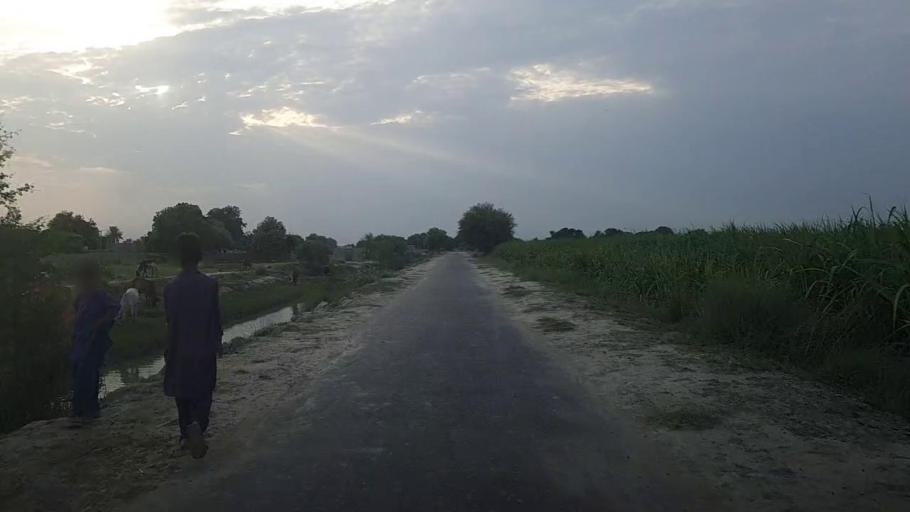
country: PK
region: Sindh
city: Ubauro
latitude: 28.3589
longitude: 69.7863
